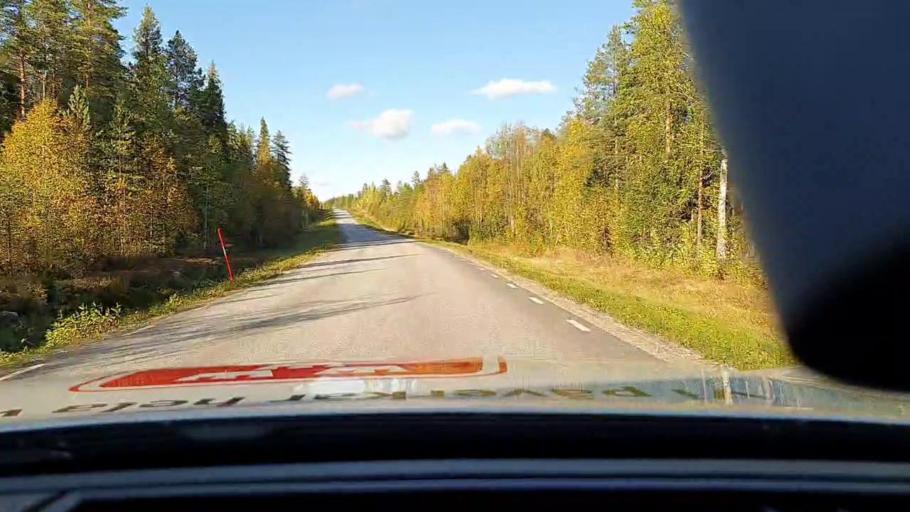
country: SE
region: Norrbotten
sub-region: Pitea Kommun
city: Norrfjarden
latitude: 65.4914
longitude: 21.4726
